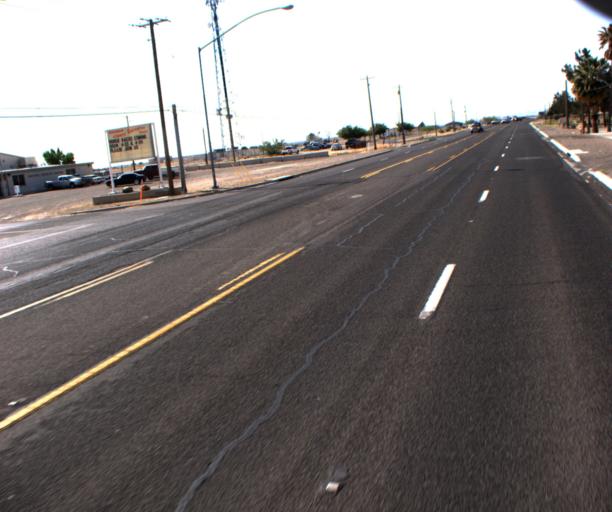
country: US
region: Arizona
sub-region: Graham County
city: Cactus Flat
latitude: 32.7954
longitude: -109.7078
